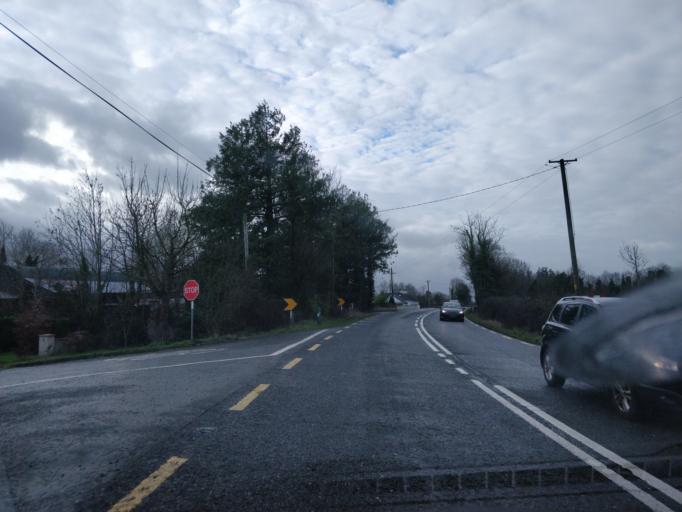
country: IE
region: Connaught
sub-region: Roscommon
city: Roscommon
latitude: 53.7694
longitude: -8.1521
